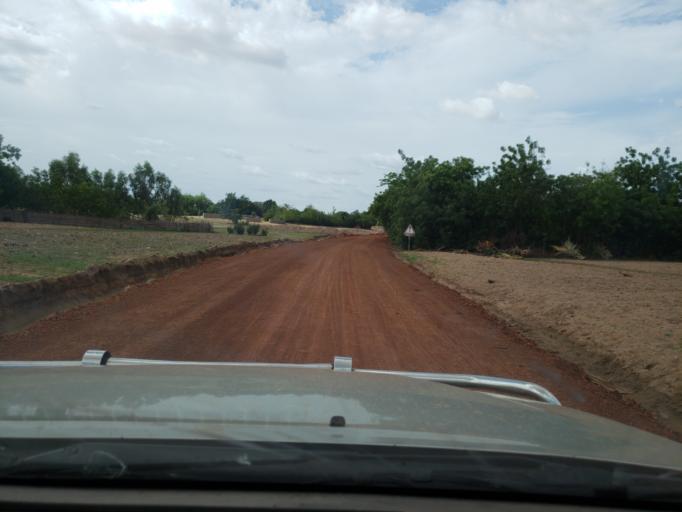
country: ML
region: Segou
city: Bla
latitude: 12.7268
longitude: -5.6735
